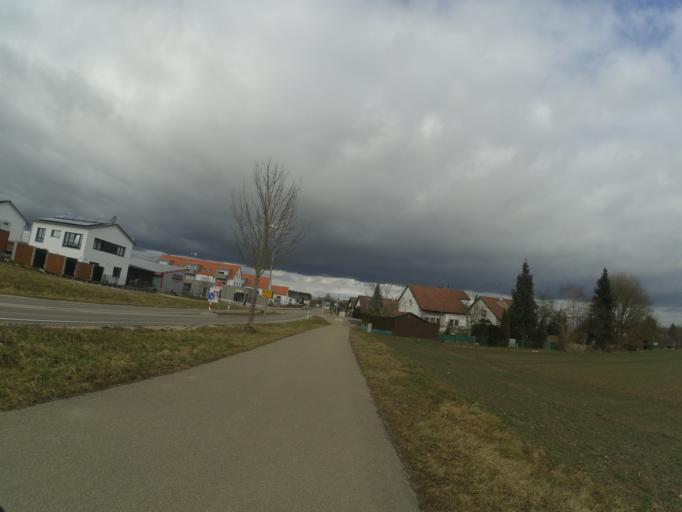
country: DE
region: Bavaria
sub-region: Swabia
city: Vohringen
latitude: 48.3116
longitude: 10.1024
